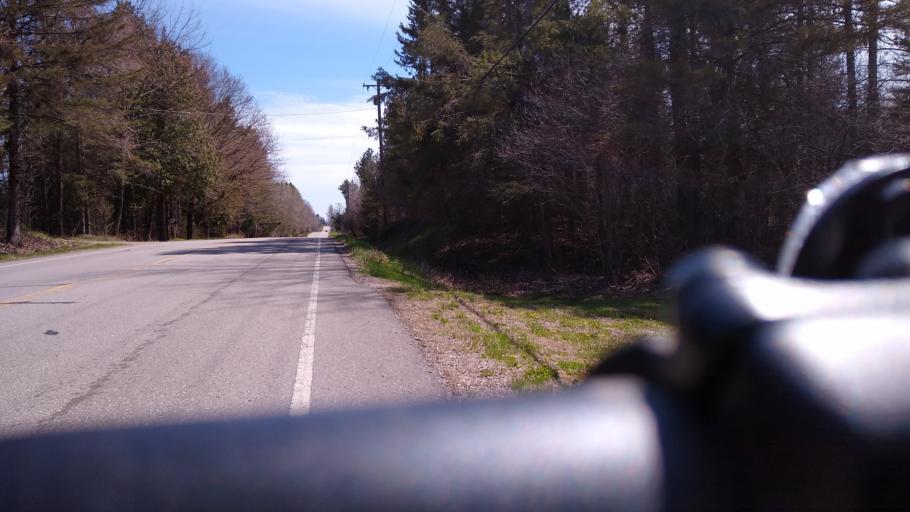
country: US
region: Michigan
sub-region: Delta County
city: Escanaba
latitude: 45.7309
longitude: -87.2025
